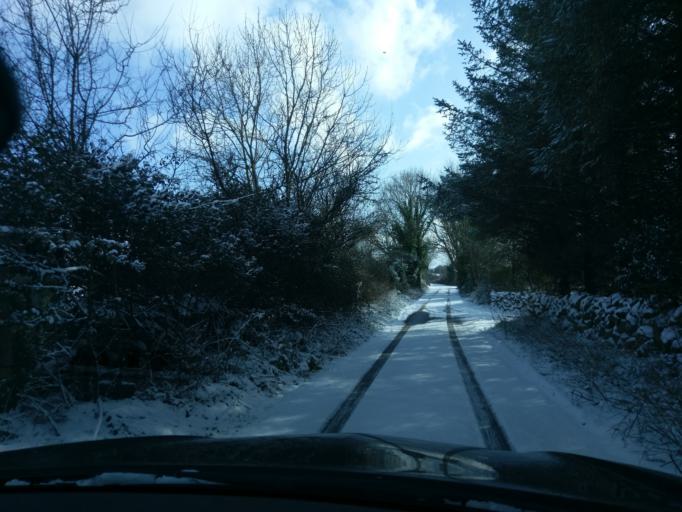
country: IE
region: Connaught
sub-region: County Galway
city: Athenry
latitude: 53.2178
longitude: -8.7690
